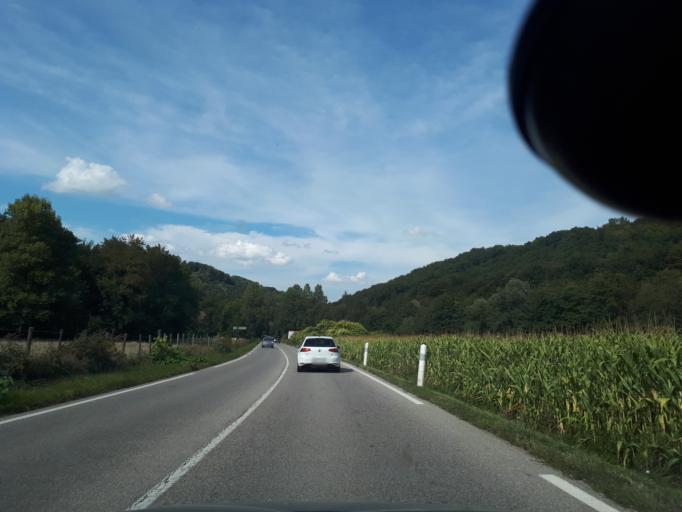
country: FR
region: Rhone-Alpes
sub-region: Departement de l'Isere
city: Maubec
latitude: 45.5568
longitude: 5.2747
